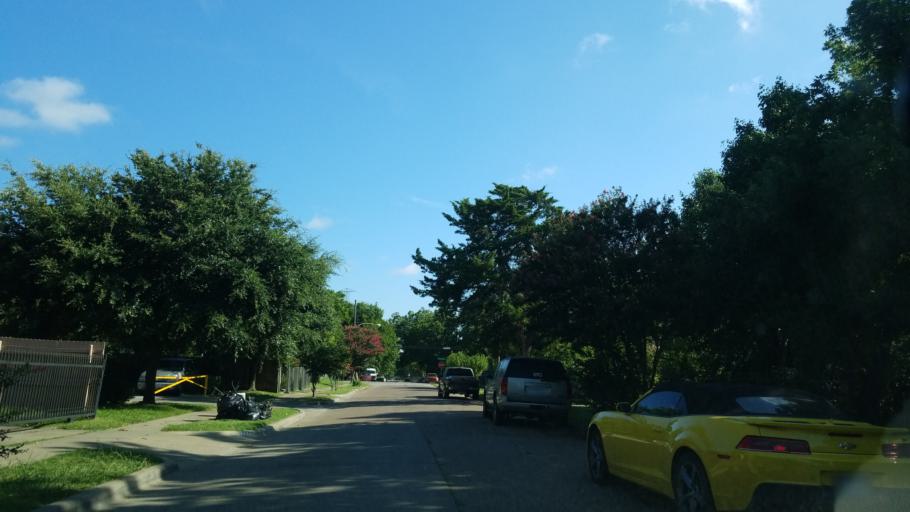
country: US
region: Texas
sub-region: Dallas County
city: Dallas
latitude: 32.7140
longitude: -96.8098
